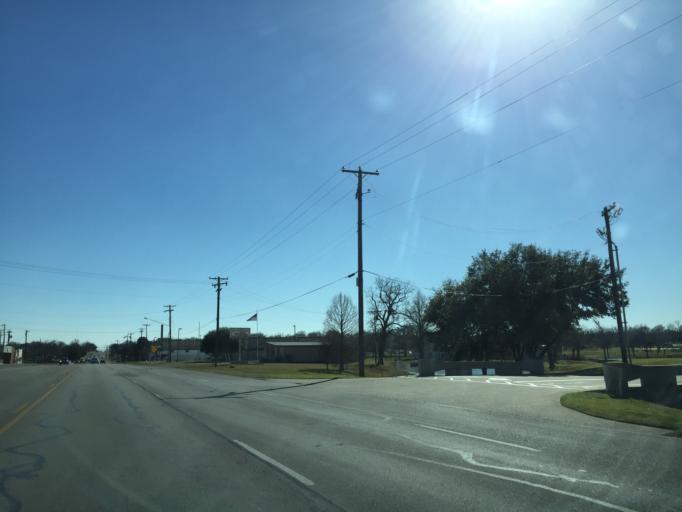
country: US
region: Texas
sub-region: Williamson County
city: Taylor
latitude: 30.5827
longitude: -97.4111
